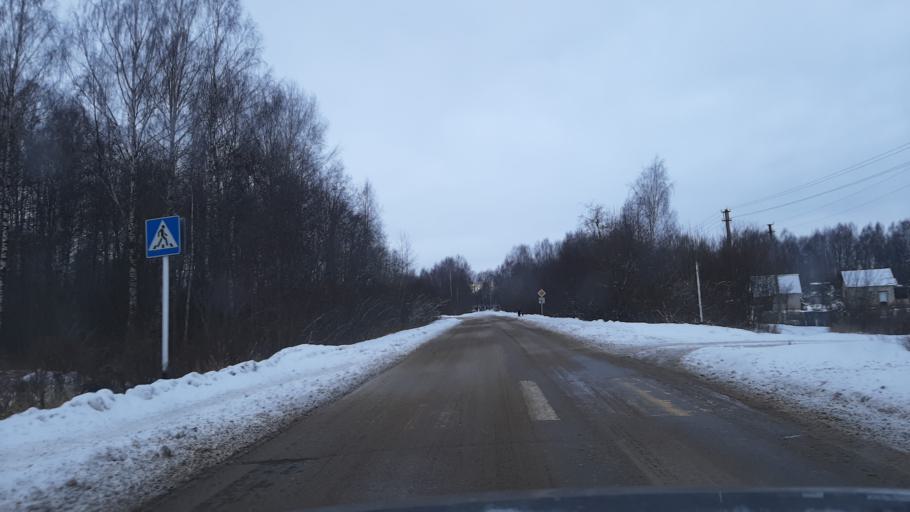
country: RU
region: Kostroma
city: Volgorechensk
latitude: 57.4449
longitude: 41.1367
